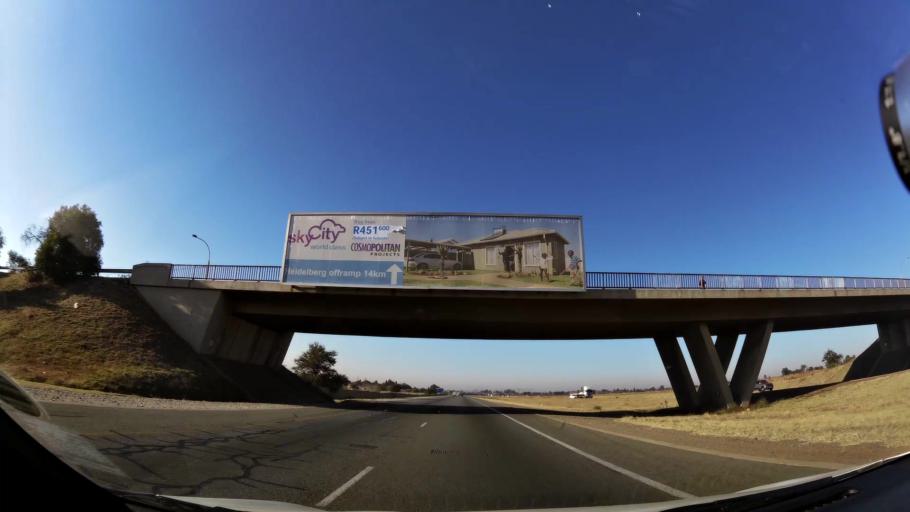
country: ZA
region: Gauteng
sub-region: Ekurhuleni Metropolitan Municipality
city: Germiston
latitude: -26.2949
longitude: 28.1063
